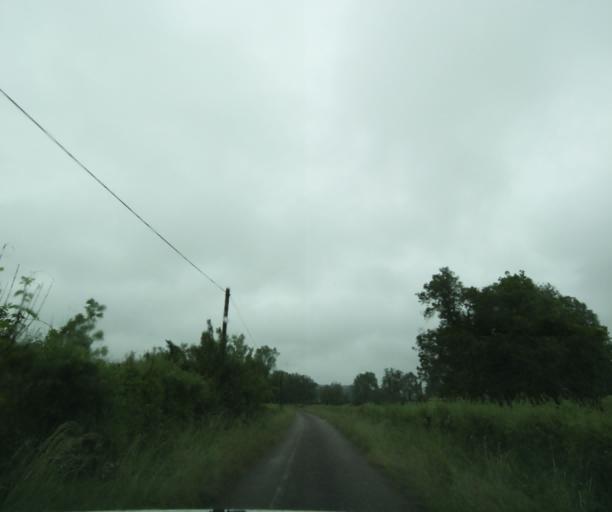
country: FR
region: Bourgogne
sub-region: Departement de Saone-et-Loire
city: Charolles
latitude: 46.3904
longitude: 4.3408
